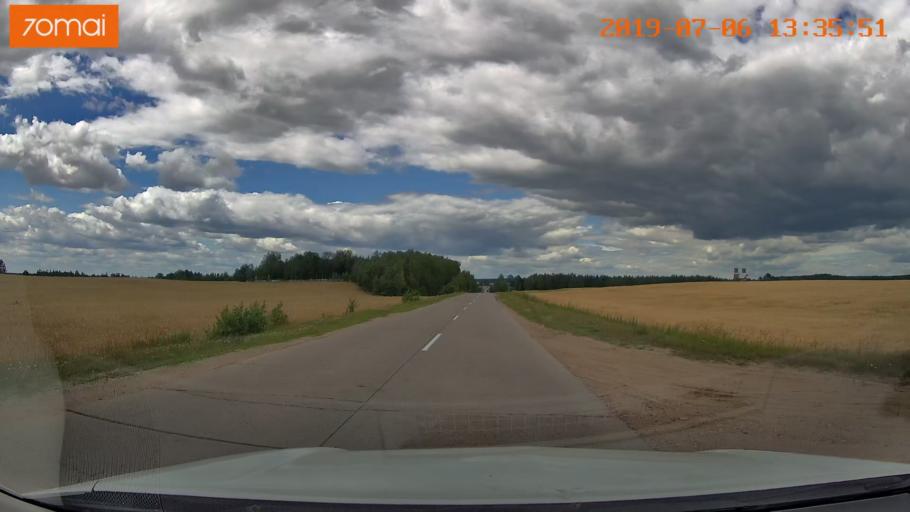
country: BY
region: Minsk
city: Enyerhyetykaw
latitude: 53.6849
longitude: 26.8739
